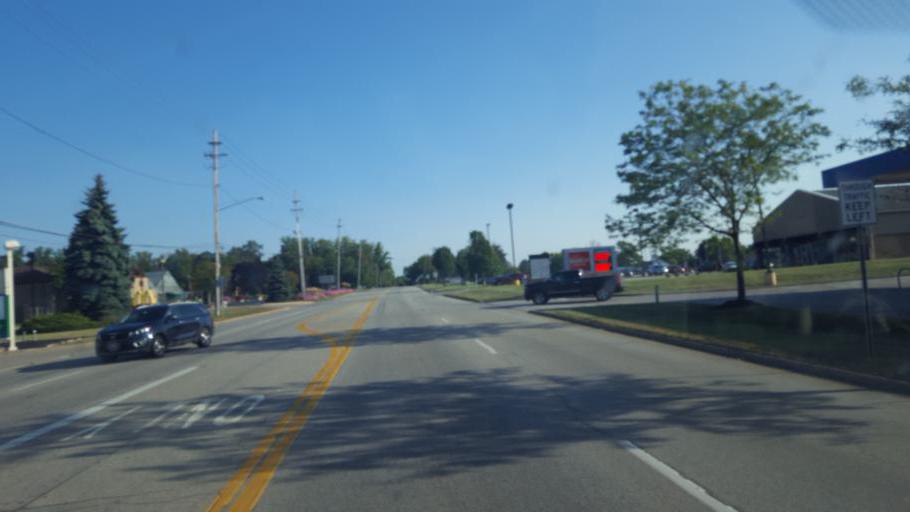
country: US
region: Ohio
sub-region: Geauga County
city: Bainbridge
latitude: 41.3893
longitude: -81.3391
